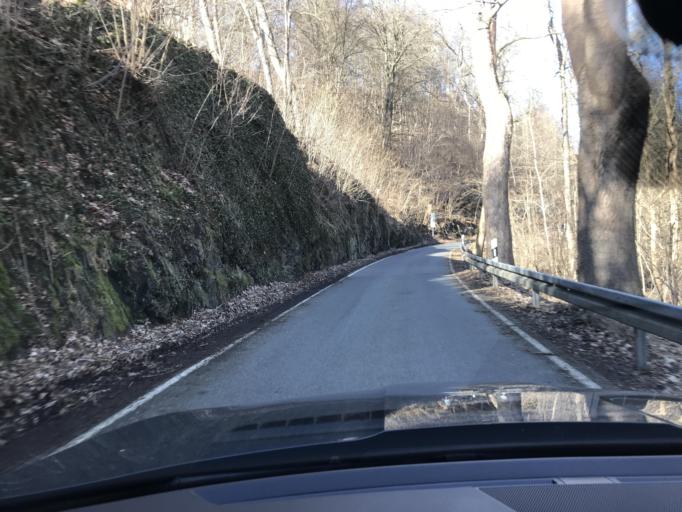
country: DE
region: Saxony-Anhalt
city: Timmenrode
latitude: 51.7171
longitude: 10.9735
